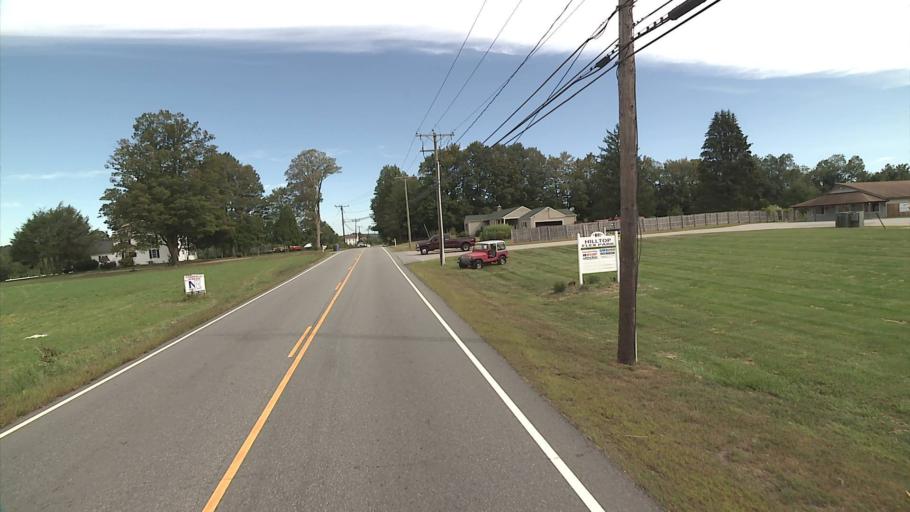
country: US
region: Connecticut
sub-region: Windham County
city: South Windham
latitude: 41.6437
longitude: -72.1612
